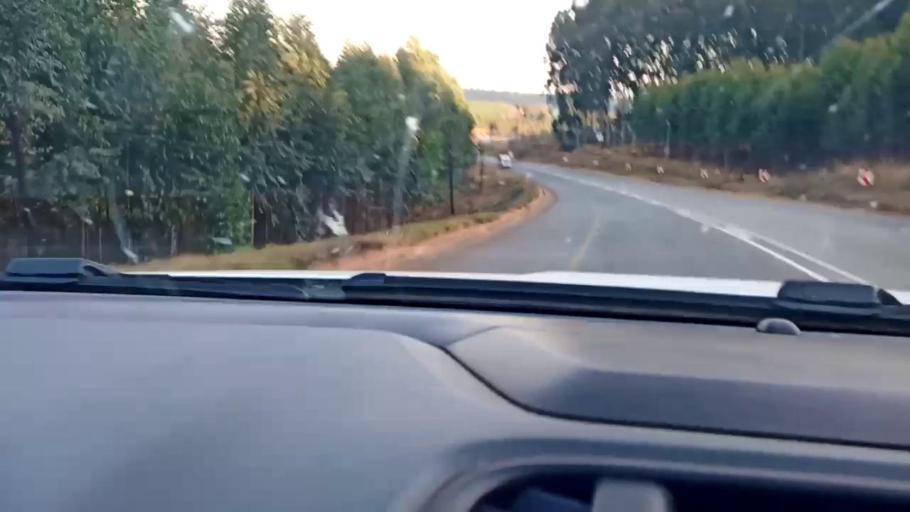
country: ZA
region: Limpopo
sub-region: Mopani District Municipality
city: Duiwelskloof
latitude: -23.7075
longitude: 30.1308
